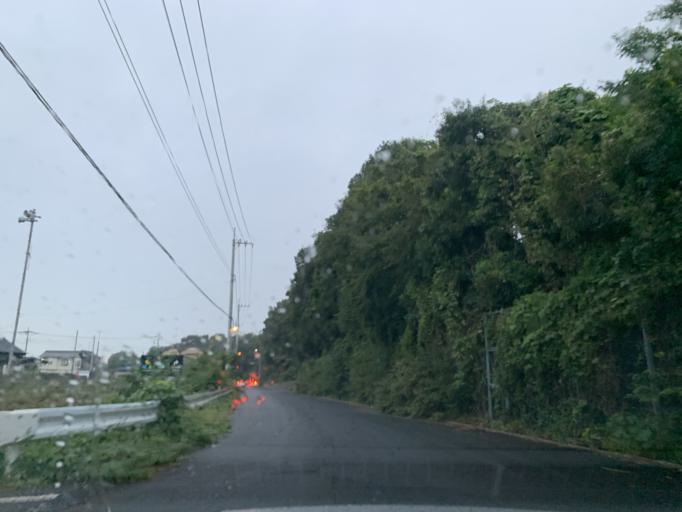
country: JP
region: Chiba
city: Nagareyama
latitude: 35.8642
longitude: 139.8834
